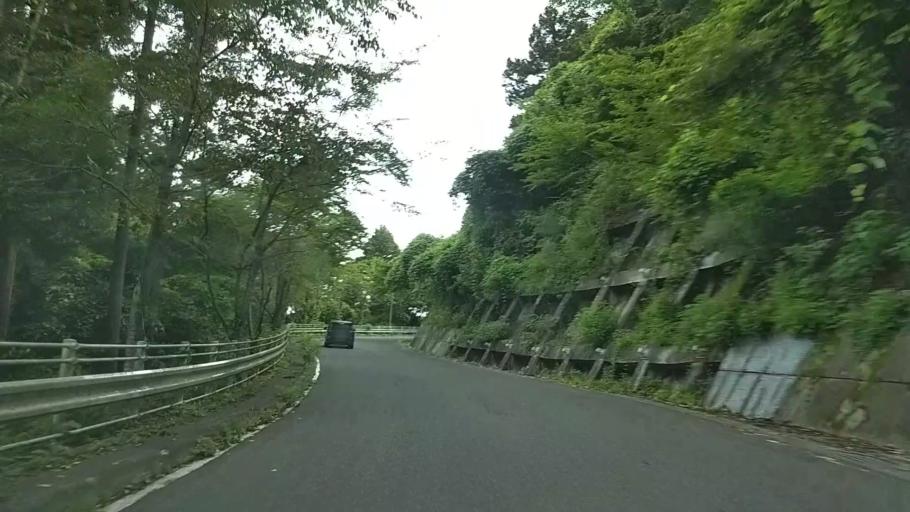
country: JP
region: Yamanashi
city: Uenohara
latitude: 35.5452
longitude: 139.1368
